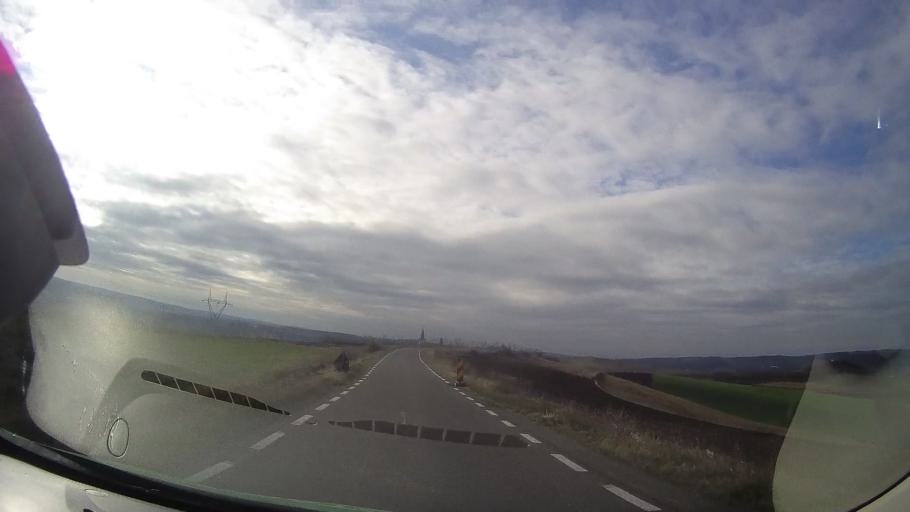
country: RO
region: Mures
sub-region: Comuna Sanger
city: Sanger
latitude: 46.5482
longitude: 24.1549
